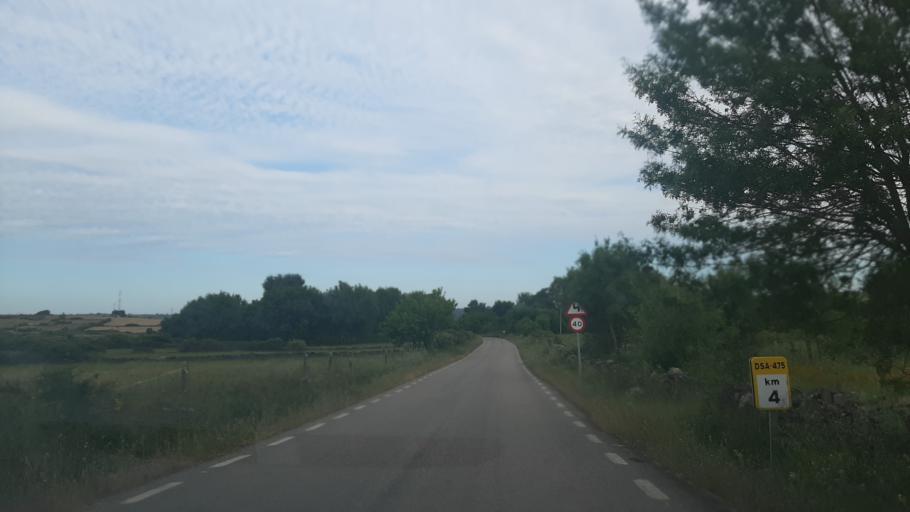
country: ES
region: Castille and Leon
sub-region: Provincia de Salamanca
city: Gallegos de Arganan
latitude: 40.6458
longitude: -6.7476
